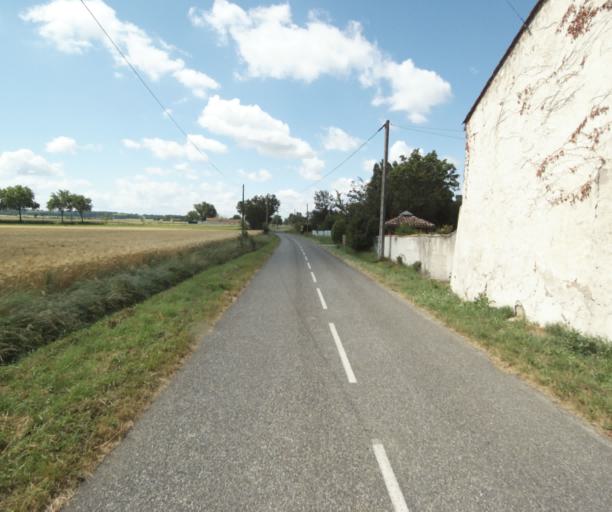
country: FR
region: Midi-Pyrenees
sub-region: Departement de la Haute-Garonne
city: Saint-Felix-Lauragais
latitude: 43.4509
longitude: 1.9174
